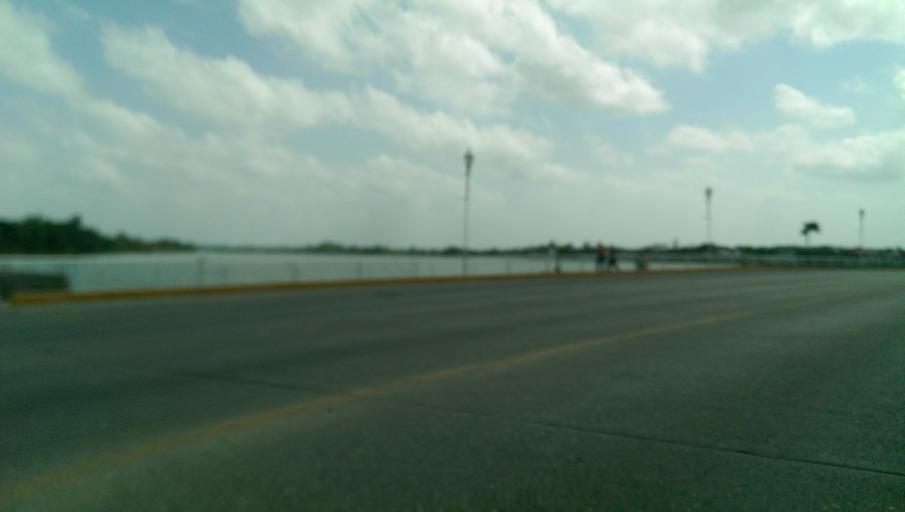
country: MX
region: Veracruz
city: Tuxpan de Rodriguez Cano
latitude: 20.9514
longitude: -97.4144
